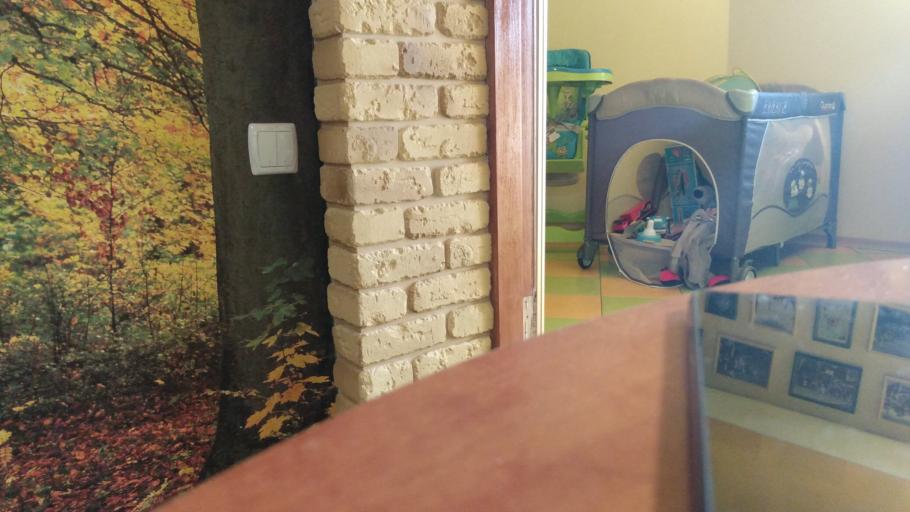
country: RU
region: Tverskaya
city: Bologoye
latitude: 57.8577
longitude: 34.3321
